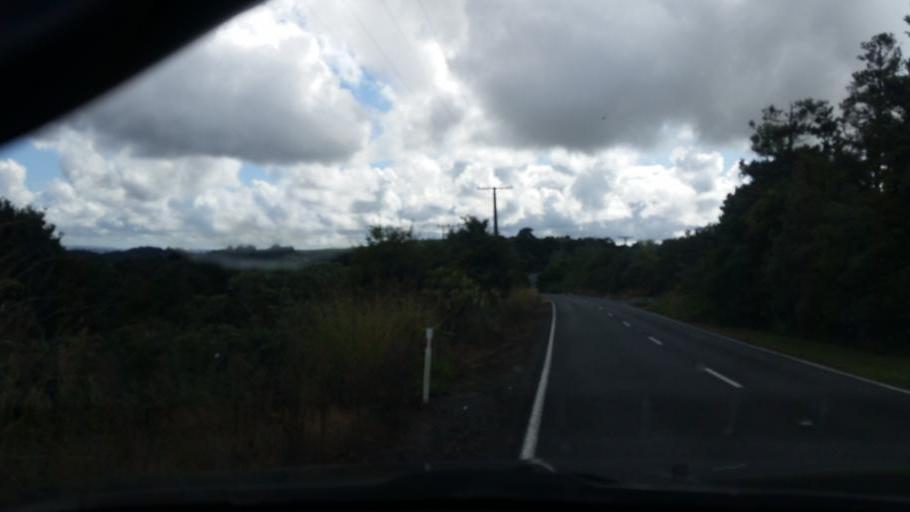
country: NZ
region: Northland
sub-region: Whangarei
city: Ruakaka
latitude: -36.0757
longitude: 174.2589
